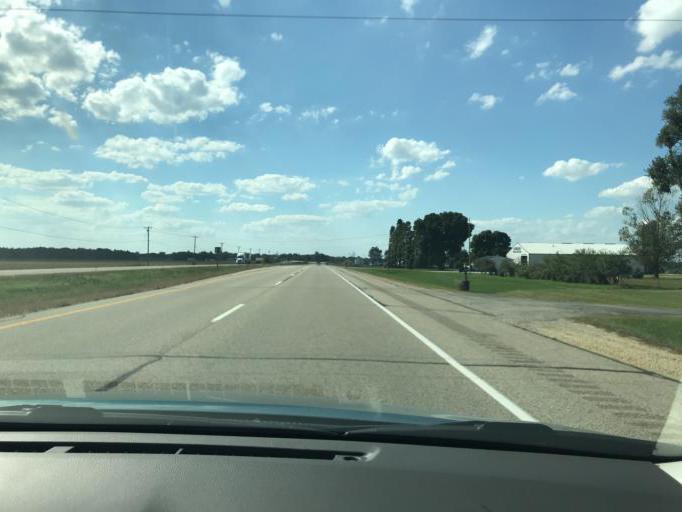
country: US
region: Wisconsin
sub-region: Kenosha County
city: Powers Lake
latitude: 42.5817
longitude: -88.3196
